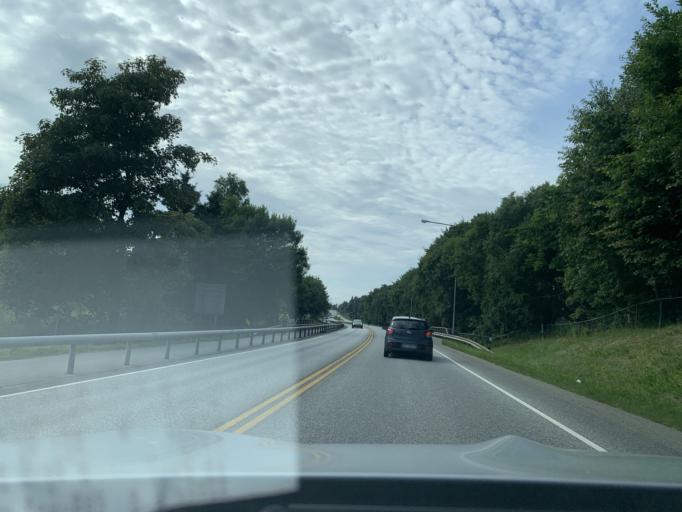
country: NO
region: Rogaland
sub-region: Stavanger
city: Stavanger
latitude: 58.9154
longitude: 5.7218
